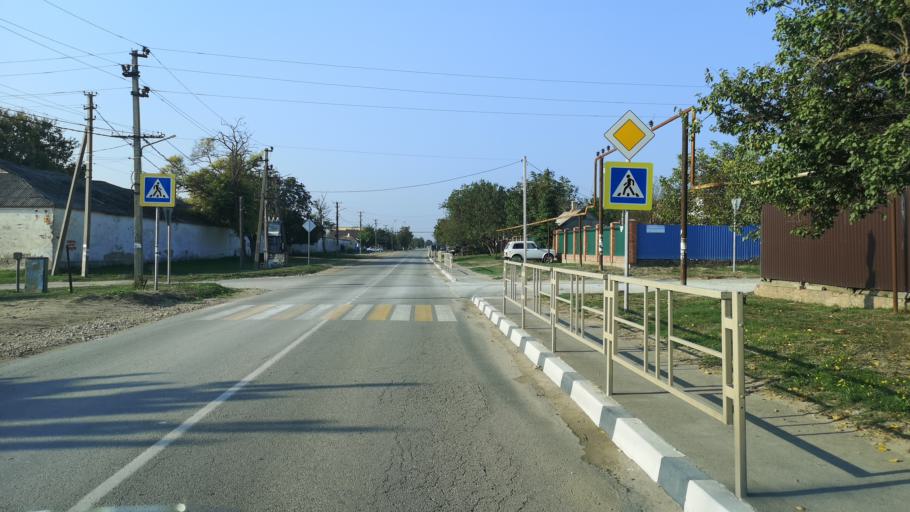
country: RU
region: Krasnodarskiy
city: Taman'
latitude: 45.2103
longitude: 36.6976
